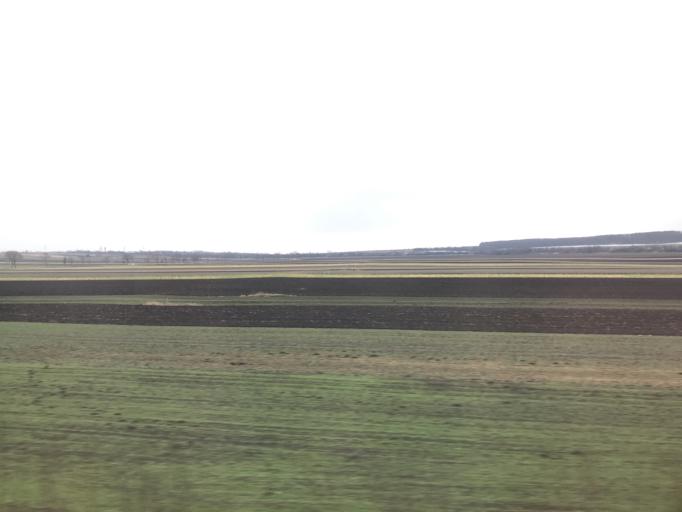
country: AT
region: Burgenland
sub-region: Politischer Bezirk Neusiedl am See
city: Parndorf
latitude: 47.9952
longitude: 16.8425
